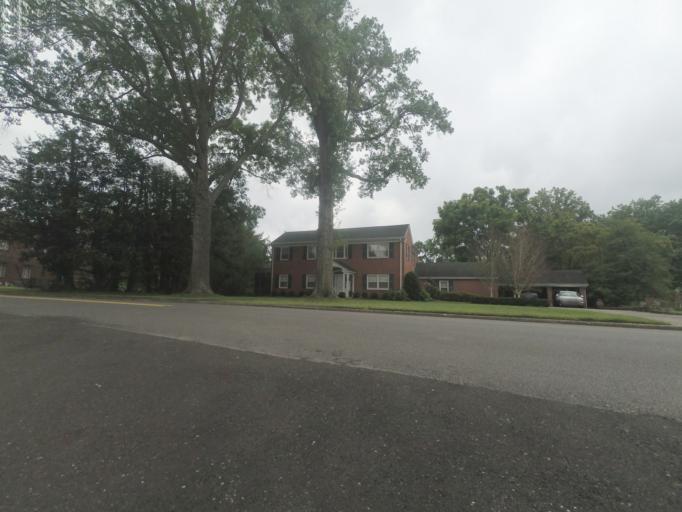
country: US
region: West Virginia
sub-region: Cabell County
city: Huntington
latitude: 38.4048
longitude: -82.4168
